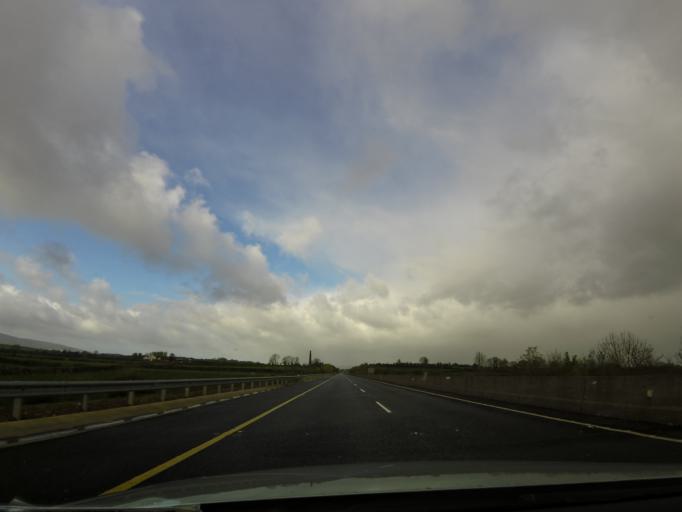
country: IE
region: Munster
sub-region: North Tipperary
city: Nenagh
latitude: 52.8462
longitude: -8.1942
